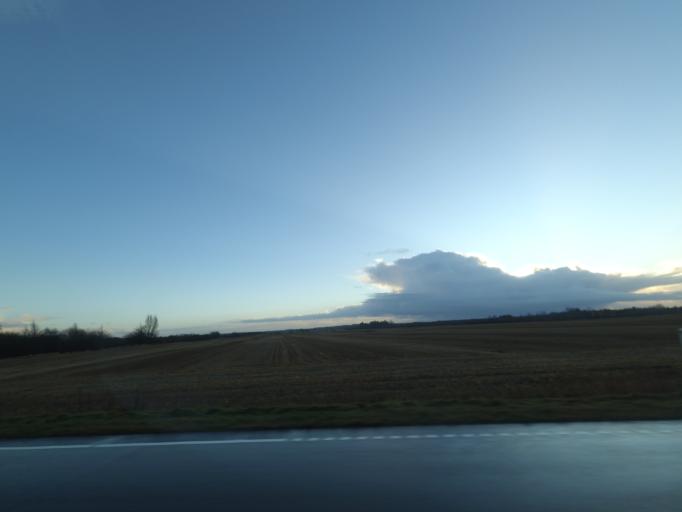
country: DK
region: Central Jutland
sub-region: Herning Kommune
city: Lind
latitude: 56.0117
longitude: 9.0402
